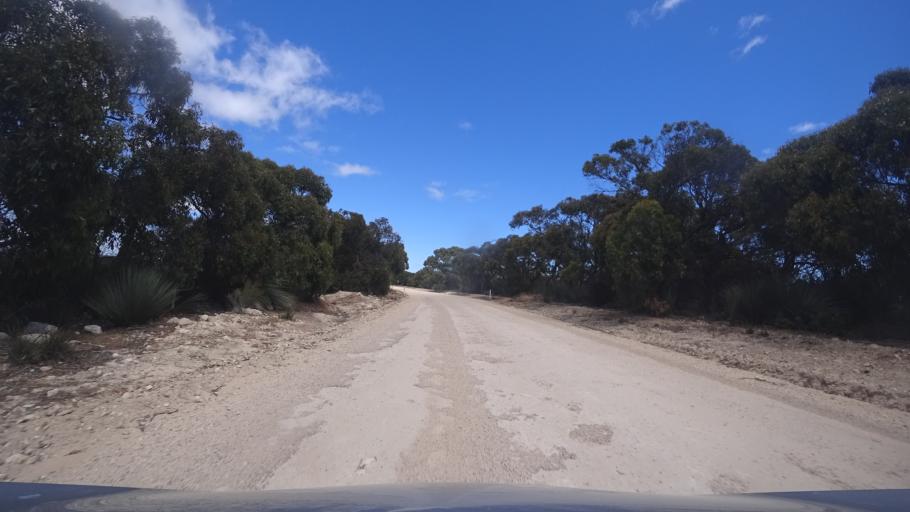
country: AU
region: South Australia
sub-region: Kangaroo Island
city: Kingscote
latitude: -35.6364
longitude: 137.2471
